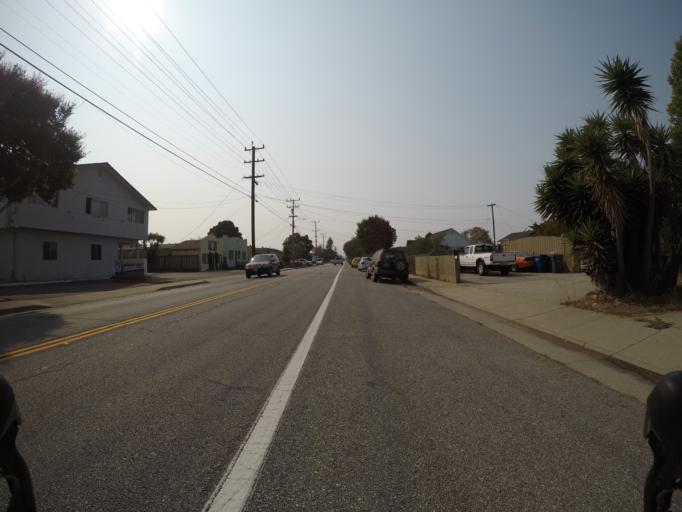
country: US
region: California
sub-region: Santa Cruz County
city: Live Oak
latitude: 36.9797
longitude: -121.9819
